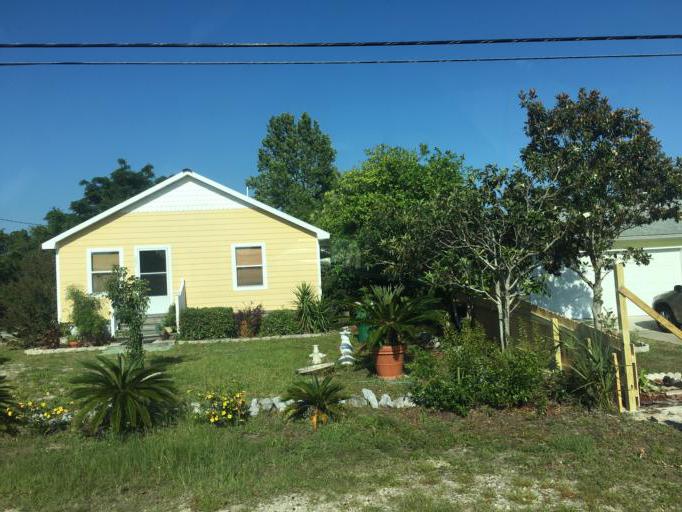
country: US
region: Florida
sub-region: Bay County
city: Panama City Beach
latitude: 30.2046
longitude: -85.8417
